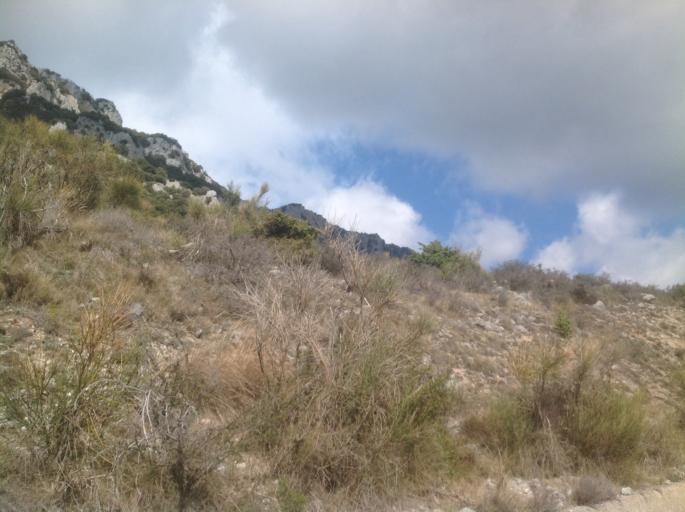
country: IT
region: Calabria
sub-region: Provincia di Cosenza
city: Civita
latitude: 39.8353
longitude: 16.3015
